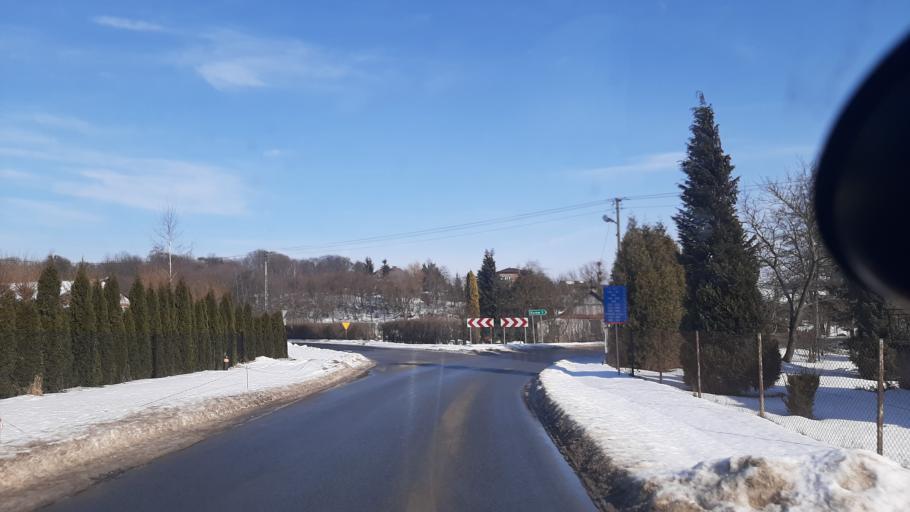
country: PL
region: Lublin Voivodeship
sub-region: Powiat pulawski
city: Wawolnica
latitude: 51.3568
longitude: 22.1214
